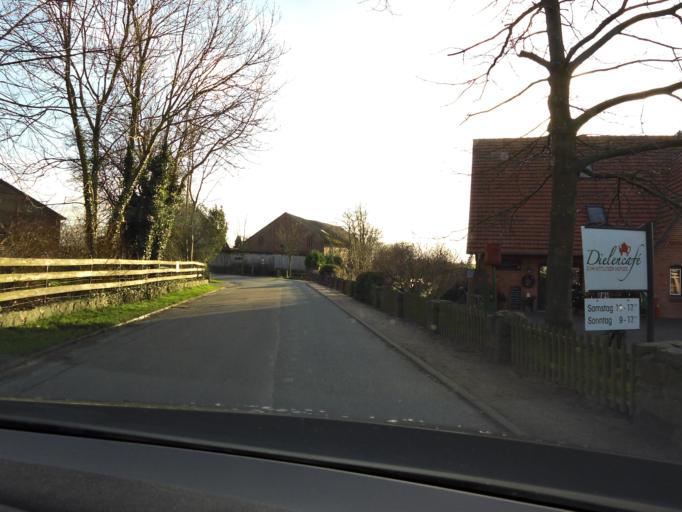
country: DE
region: Schleswig-Holstein
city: Kittlitz
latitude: 53.6641
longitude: 10.9121
